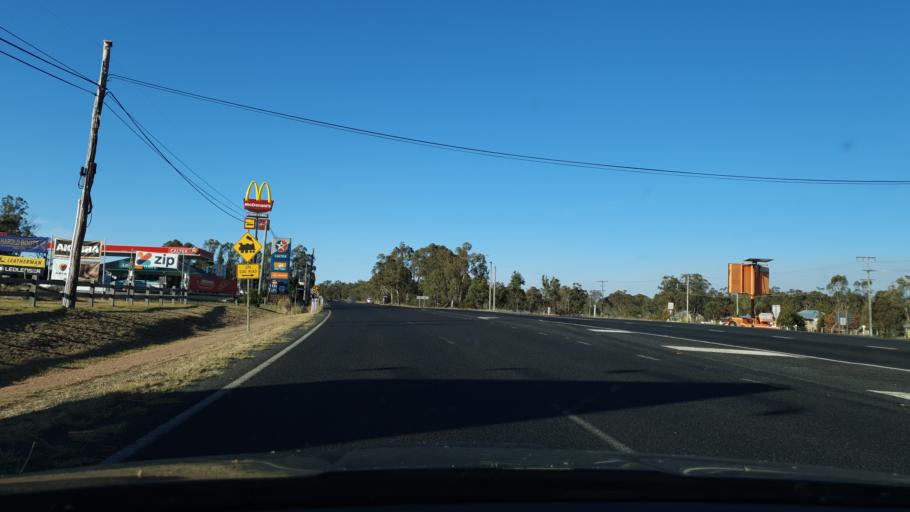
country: AU
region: Queensland
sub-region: Southern Downs
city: Stanthorpe
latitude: -28.6323
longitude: 151.9538
